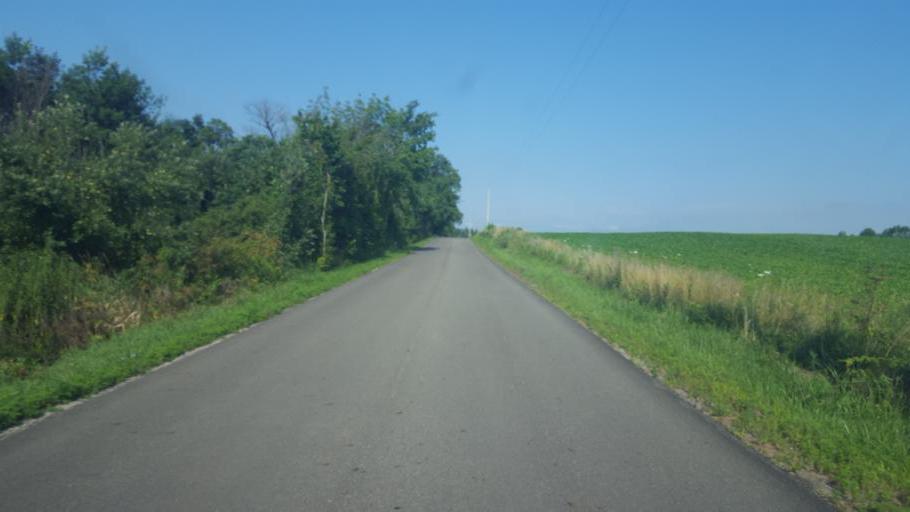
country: US
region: Ohio
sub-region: Morrow County
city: Mount Gilead
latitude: 40.6243
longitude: -82.7314
